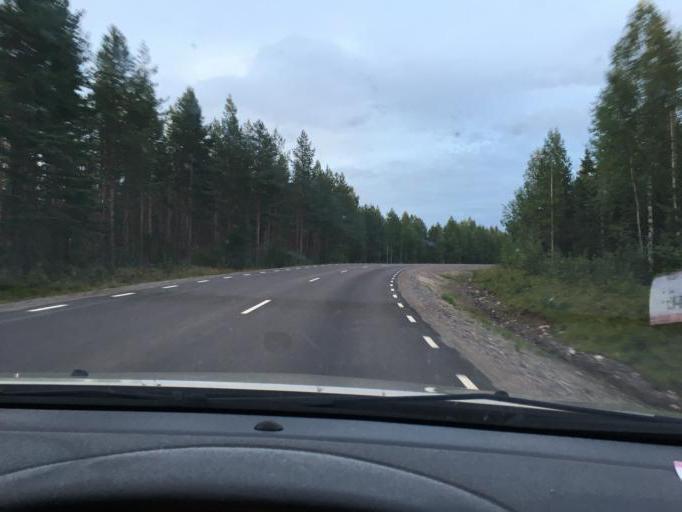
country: SE
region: Norrbotten
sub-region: Lulea Kommun
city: Ranea
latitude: 66.0524
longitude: 22.2169
